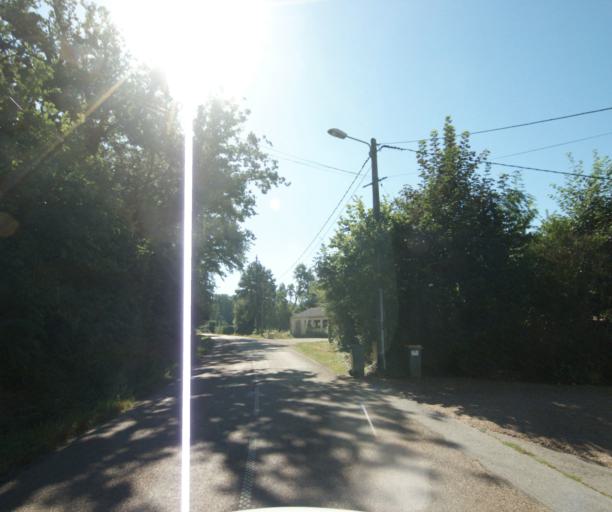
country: FR
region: Lorraine
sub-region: Departement des Vosges
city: Epinal
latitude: 48.1504
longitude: 6.4646
